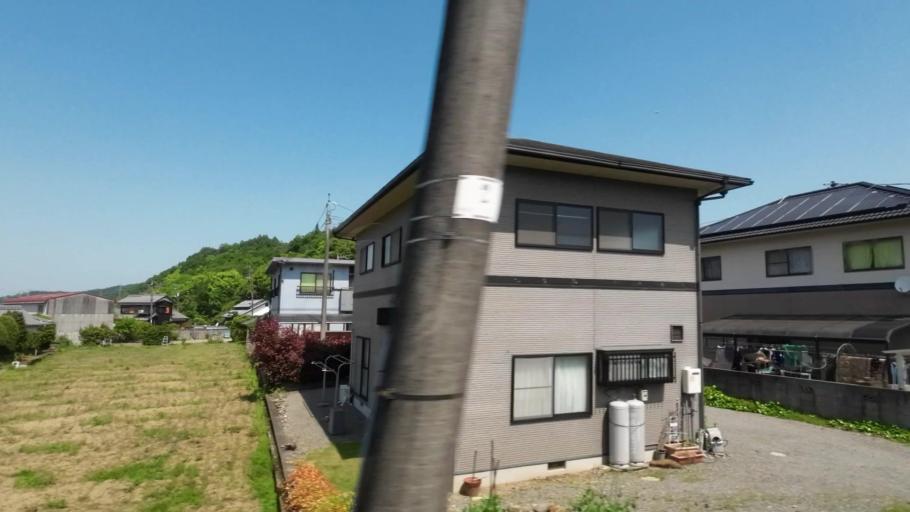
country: JP
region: Ehime
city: Niihama
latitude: 33.9255
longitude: 133.2509
